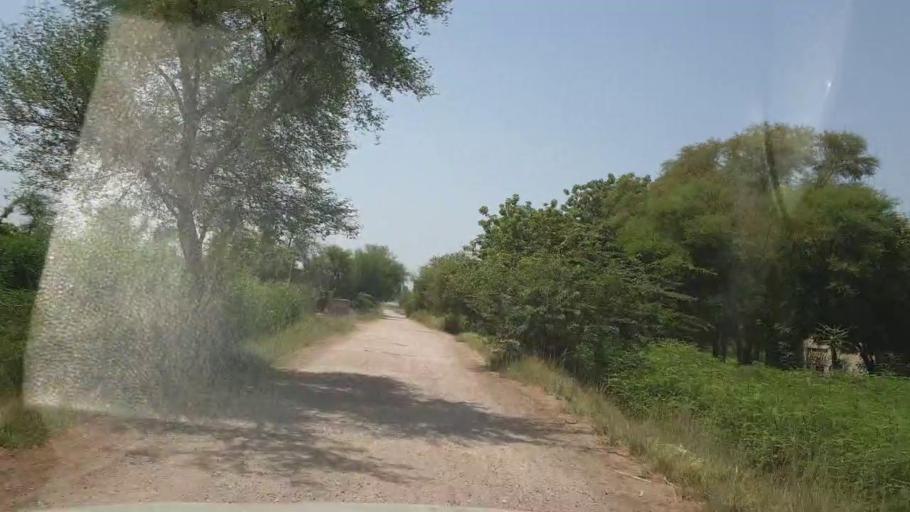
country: PK
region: Sindh
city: Bozdar
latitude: 27.1307
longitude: 68.6237
